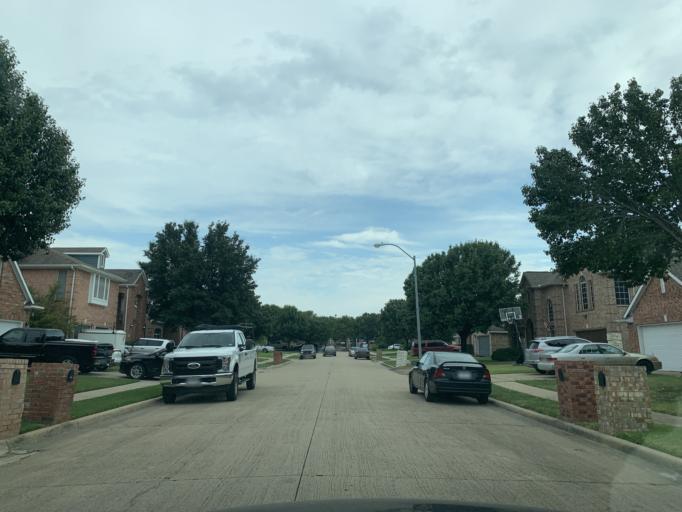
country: US
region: Texas
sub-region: Tarrant County
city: Watauga
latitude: 32.8511
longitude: -97.2894
